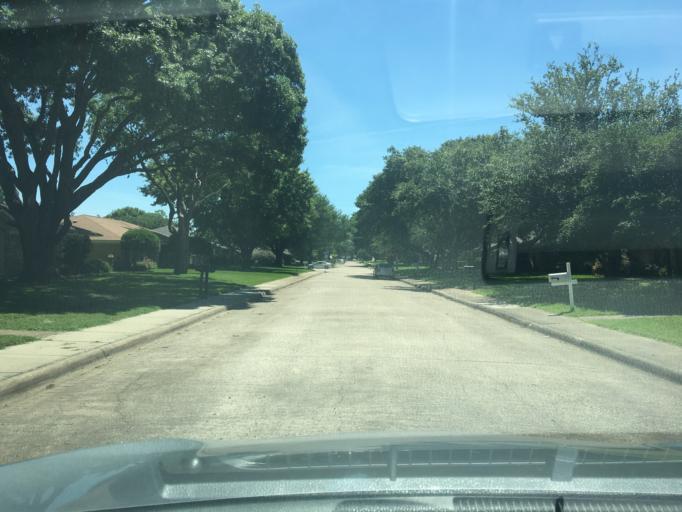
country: US
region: Texas
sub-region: Dallas County
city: Richardson
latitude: 32.9467
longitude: -96.6925
